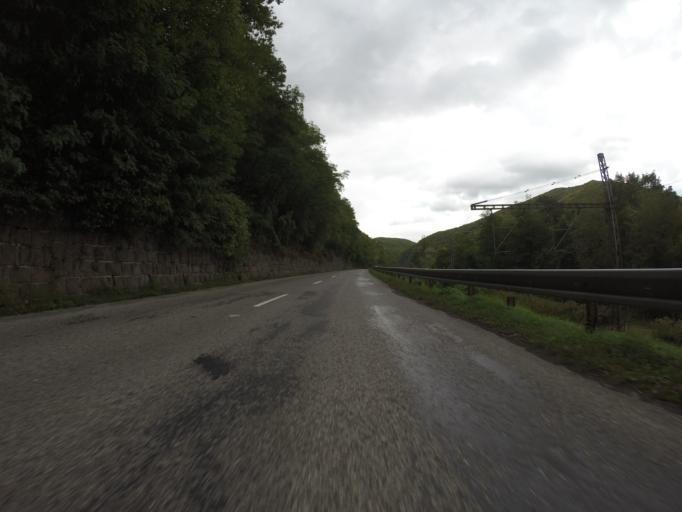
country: SK
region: Banskobystricky
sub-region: Okres Banska Bystrica
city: Zvolen
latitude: 48.5669
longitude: 19.0110
